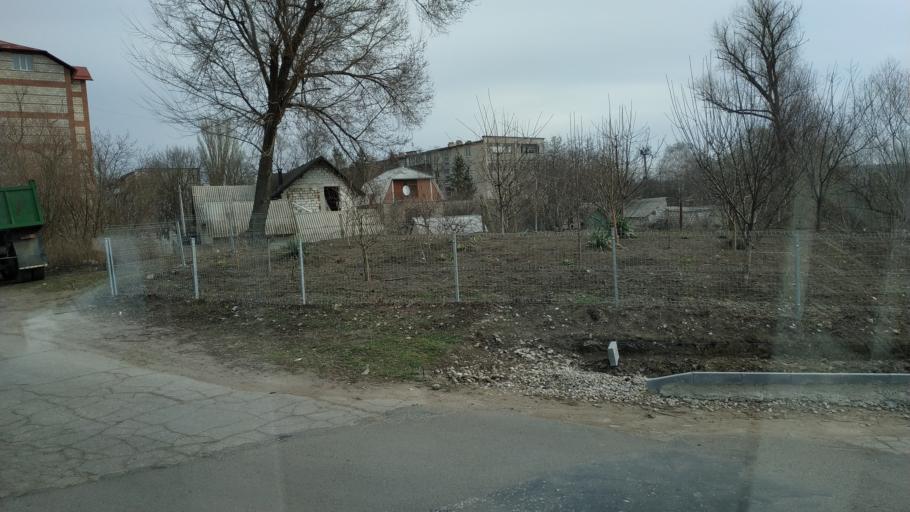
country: MD
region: Chisinau
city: Vatra
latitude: 47.0901
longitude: 28.7604
